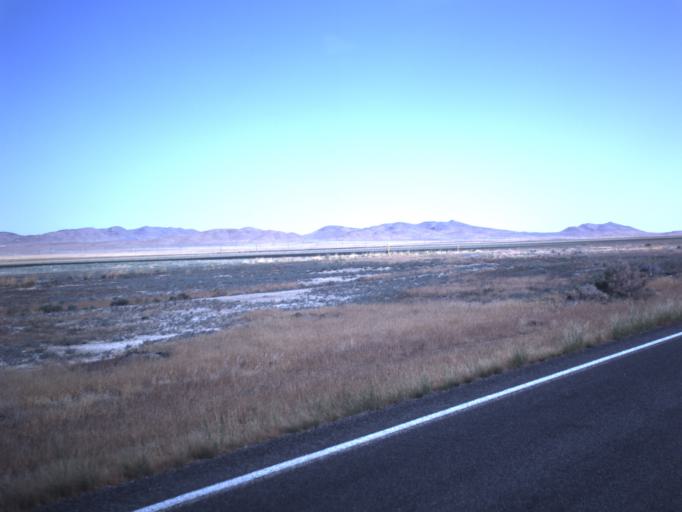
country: US
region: Utah
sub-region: Millard County
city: Delta
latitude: 38.9491
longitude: -112.8063
